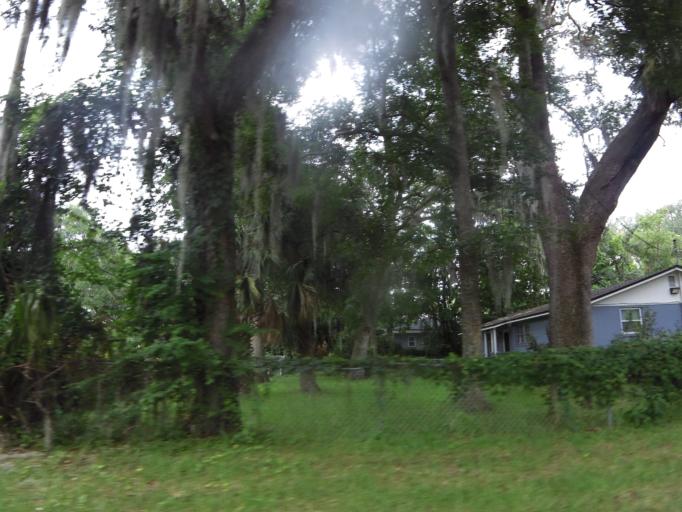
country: US
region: Florida
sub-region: Duval County
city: Atlantic Beach
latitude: 30.3349
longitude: -81.4241
